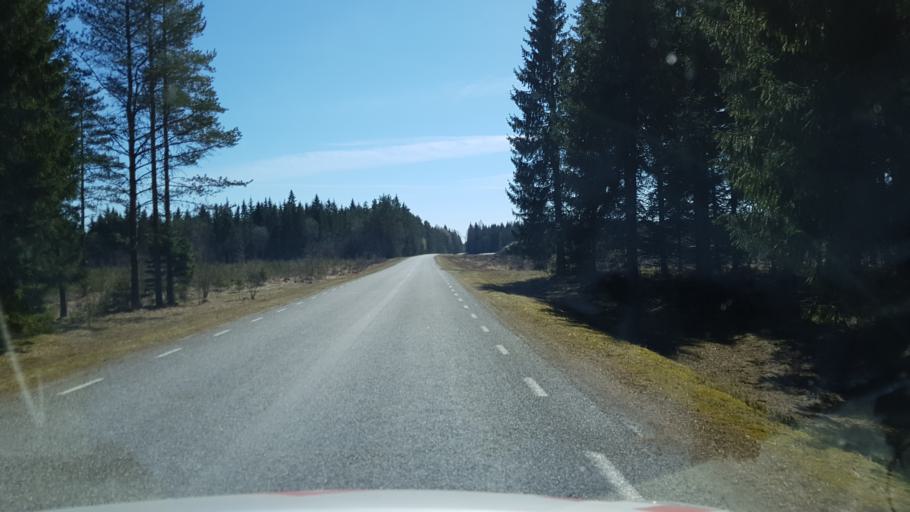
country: EE
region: Laeaene-Virumaa
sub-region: Vinni vald
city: Vinni
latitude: 59.1758
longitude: 26.5041
